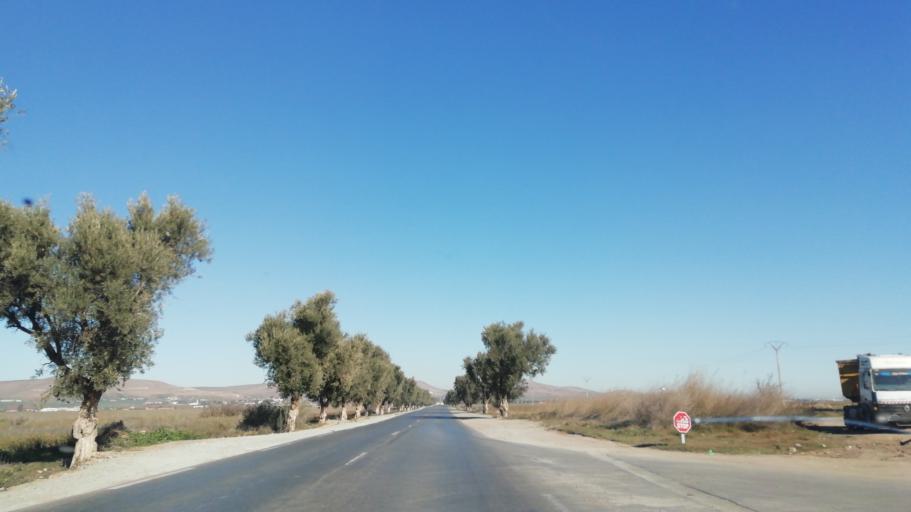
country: DZ
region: Mascara
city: Bou Hanifia el Hamamat
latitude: 35.1980
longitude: 0.1080
